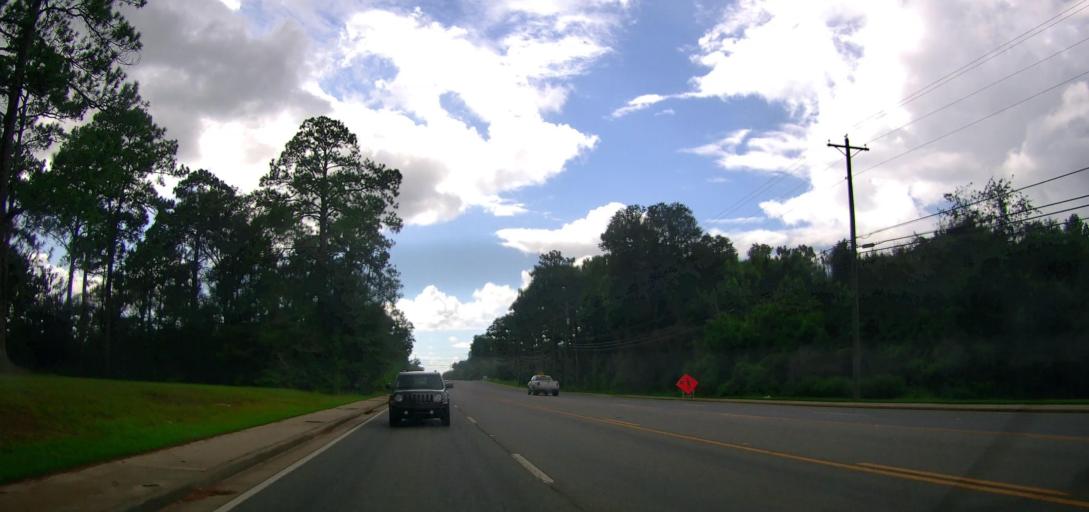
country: US
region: Georgia
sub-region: Coffee County
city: Douglas
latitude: 31.5148
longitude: -82.8768
